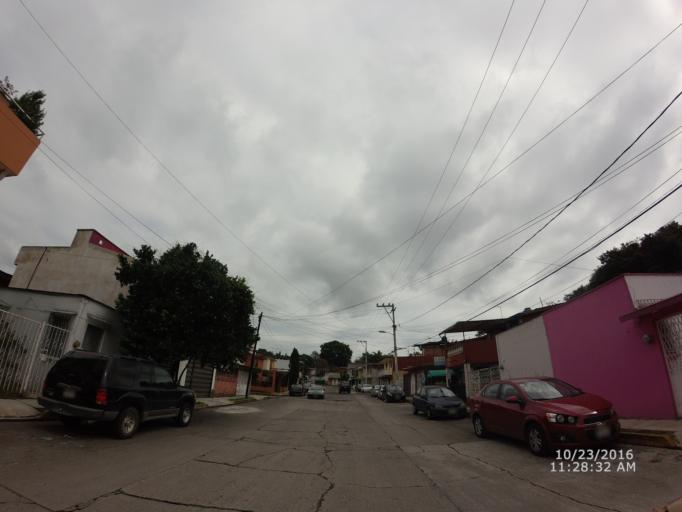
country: MX
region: Veracruz
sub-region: Tlalnelhuayocan
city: Guadalupe Victoria
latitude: 19.5470
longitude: -96.9399
